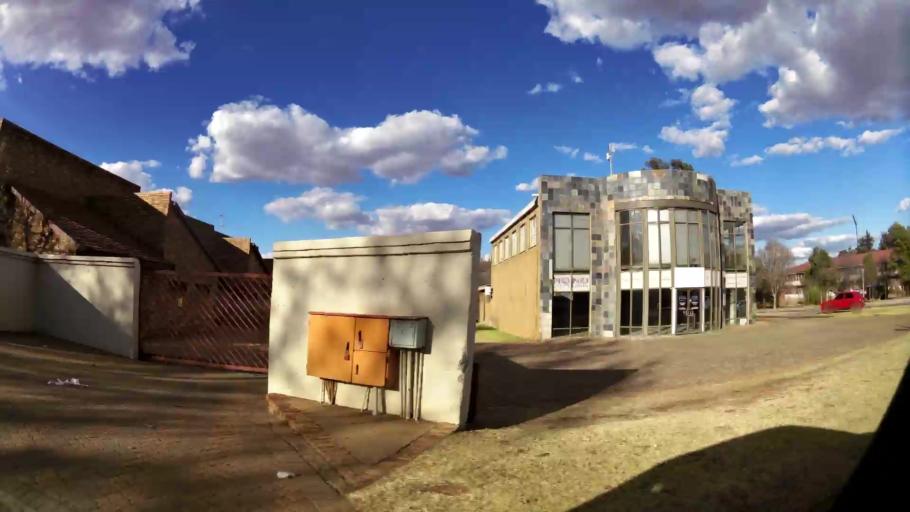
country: ZA
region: North-West
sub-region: Dr Kenneth Kaunda District Municipality
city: Potchefstroom
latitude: -26.6936
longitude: 27.0975
